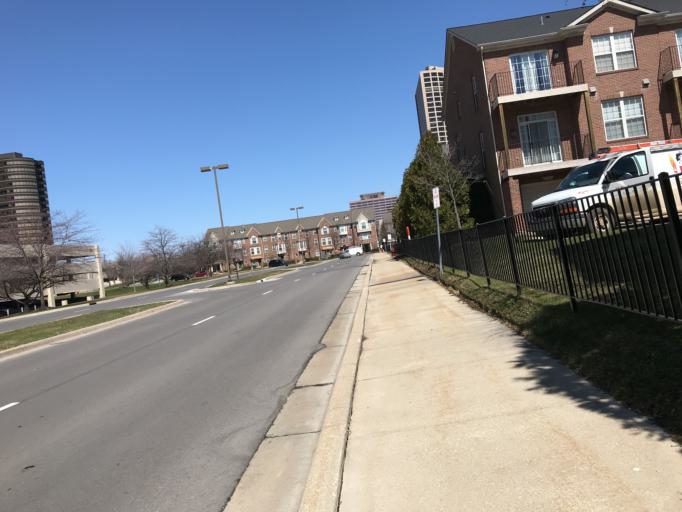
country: US
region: Michigan
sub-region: Oakland County
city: Southfield
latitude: 42.4767
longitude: -83.2428
